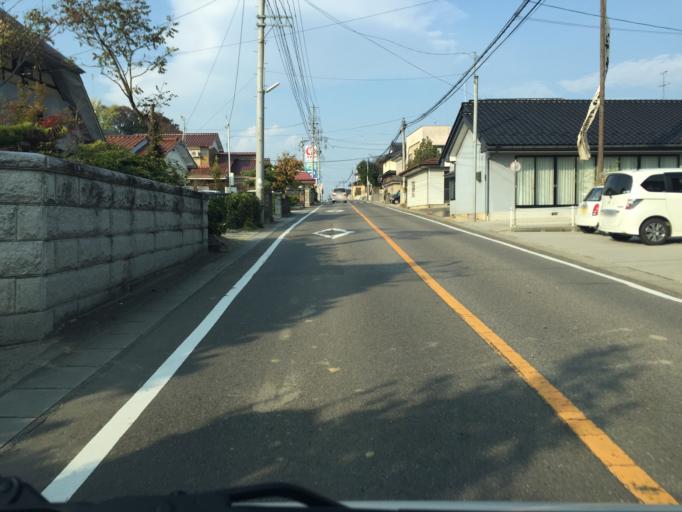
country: JP
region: Fukushima
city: Motomiya
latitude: 37.4918
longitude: 140.4011
